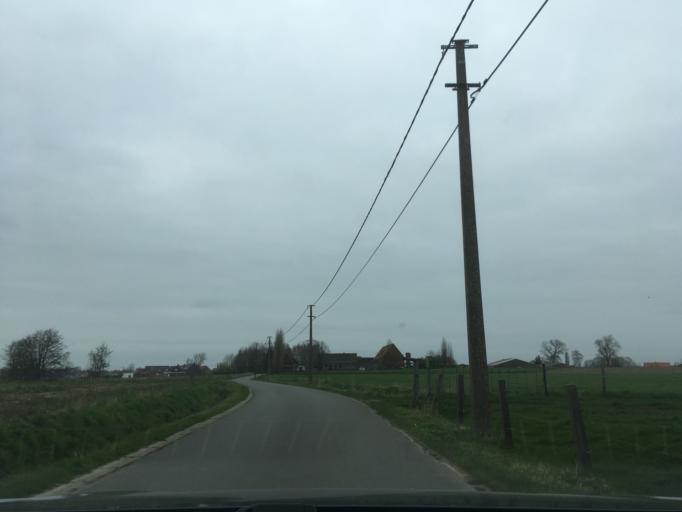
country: BE
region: Flanders
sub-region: Provincie West-Vlaanderen
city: Lichtervelde
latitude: 51.0104
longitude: 3.1524
